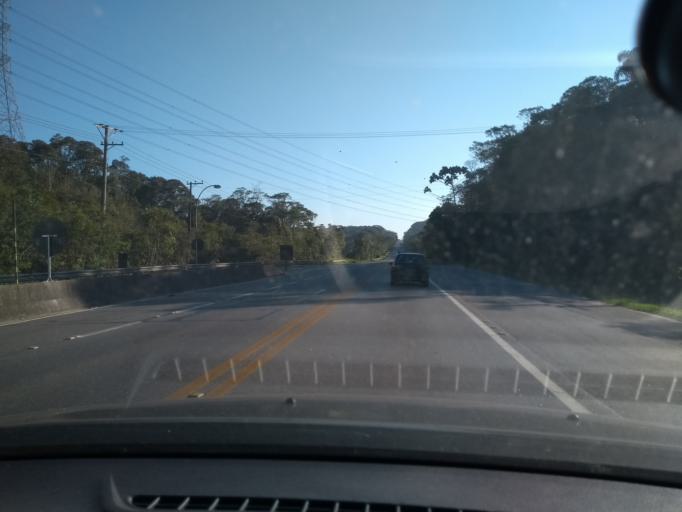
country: BR
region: Sao Paulo
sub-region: Rio Grande Da Serra
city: Rio Grande da Serra
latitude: -23.7706
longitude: -46.4731
